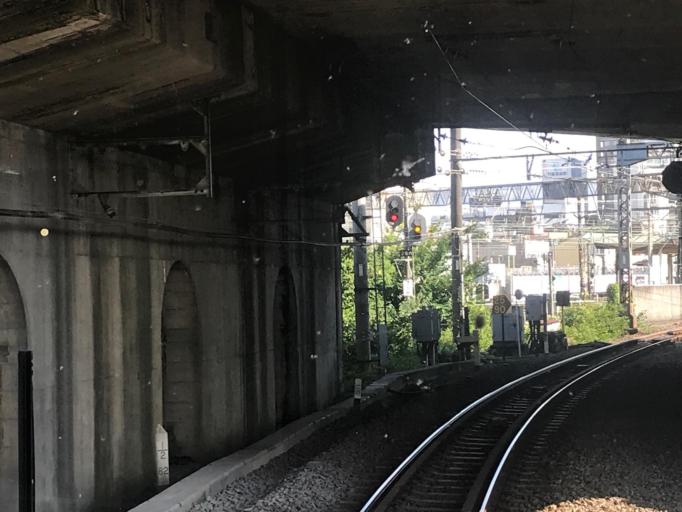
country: JP
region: Kanagawa
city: Odawara
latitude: 35.2916
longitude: 139.1473
